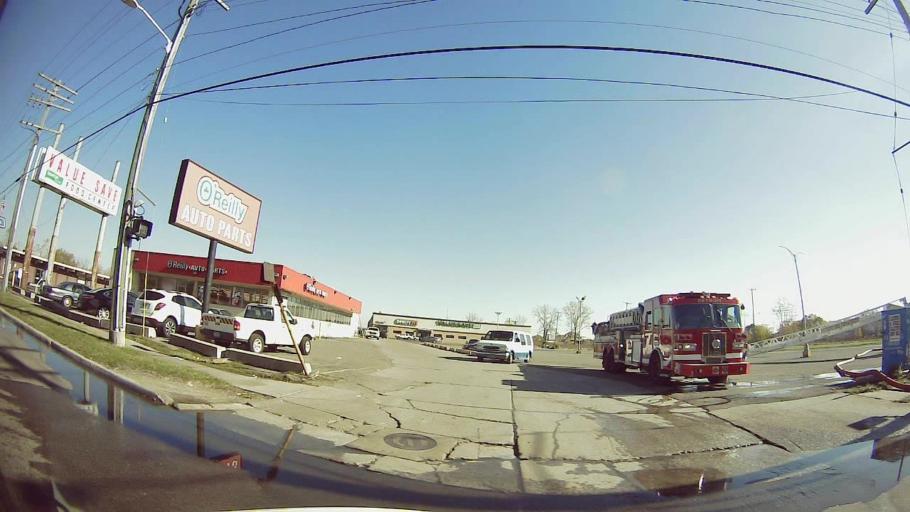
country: US
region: Michigan
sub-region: Wayne County
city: Highland Park
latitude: 42.3955
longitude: -83.1398
